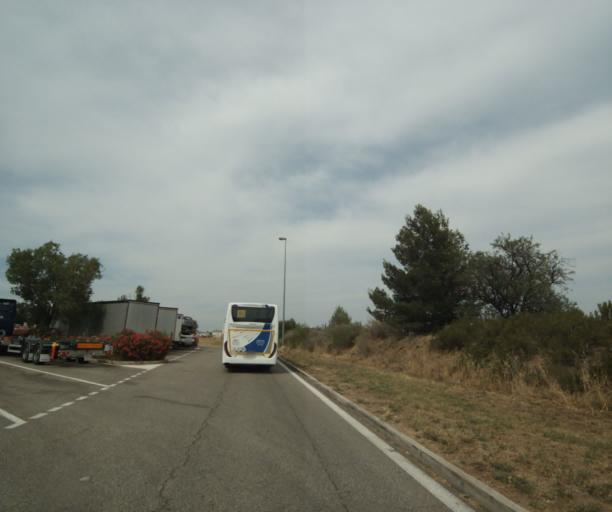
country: FR
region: Provence-Alpes-Cote d'Azur
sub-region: Departement du Var
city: La Farlede
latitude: 43.1484
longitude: 6.0336
